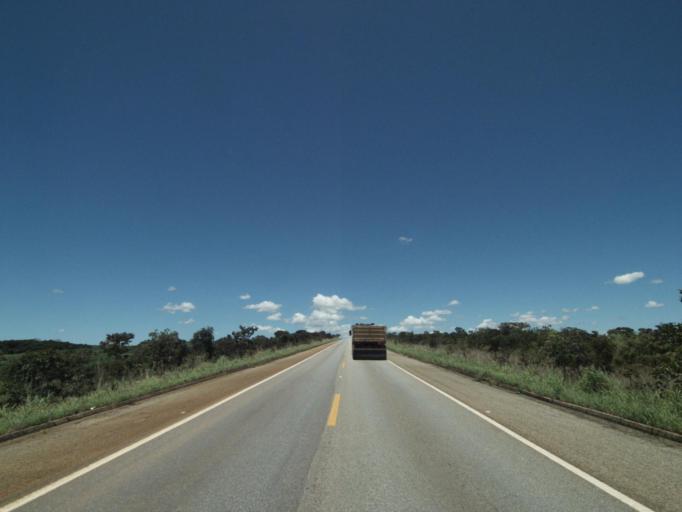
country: BR
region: Goias
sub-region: Pirenopolis
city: Pirenopolis
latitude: -15.7602
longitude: -48.6924
